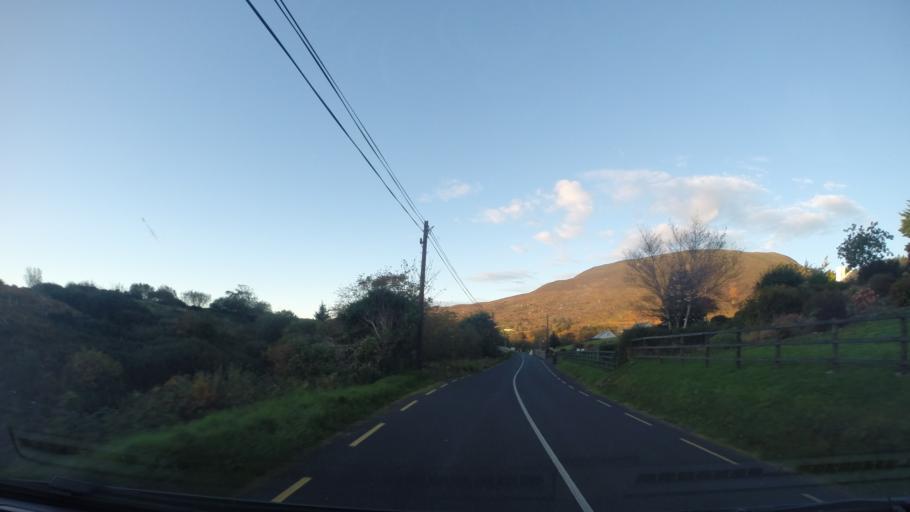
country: IE
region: Ulster
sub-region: County Donegal
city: Killybegs
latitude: 54.6535
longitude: -8.6384
